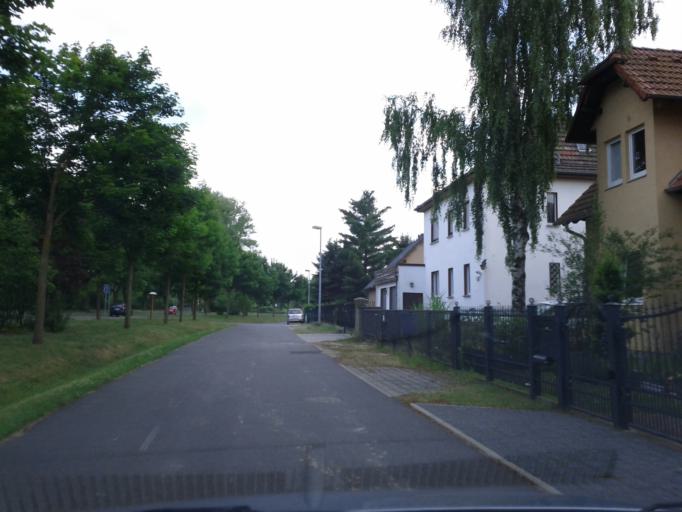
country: DE
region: Brandenburg
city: Schoneiche
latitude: 52.4700
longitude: 13.7308
